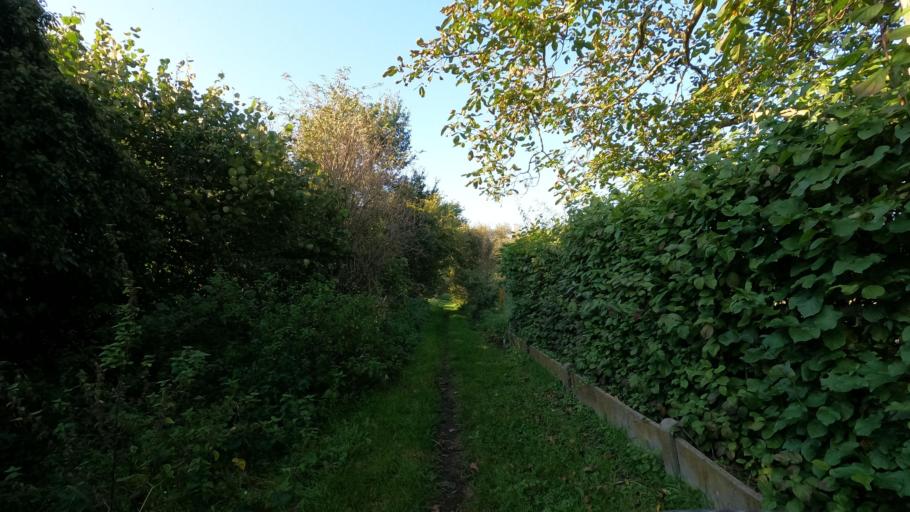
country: BE
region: Flanders
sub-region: Provincie Vlaams-Brabant
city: Rotselaar
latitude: 50.9630
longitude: 4.7078
